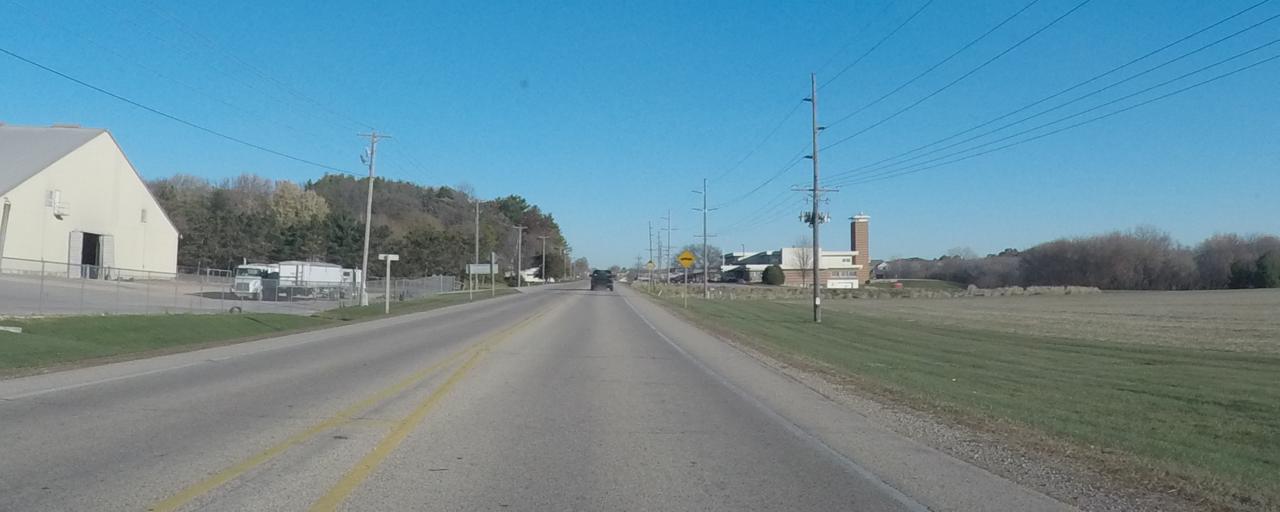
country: US
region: Wisconsin
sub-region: Dane County
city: Cottage Grove
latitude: 43.0667
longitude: -89.1997
